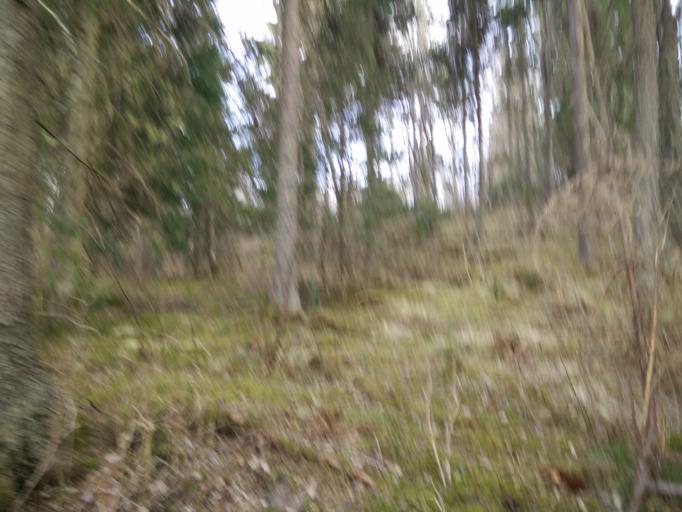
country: FI
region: Pirkanmaa
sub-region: Tampere
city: Orivesi
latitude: 61.7127
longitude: 24.3210
